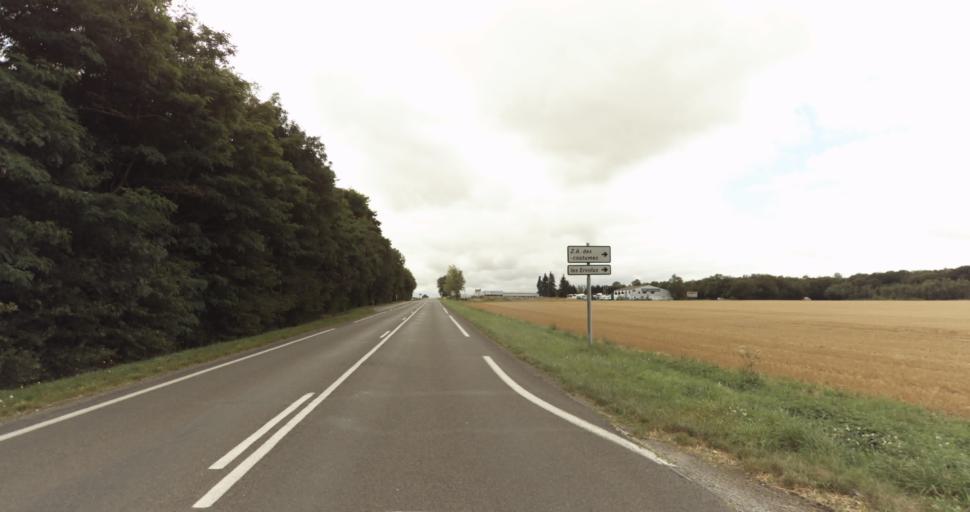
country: FR
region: Haute-Normandie
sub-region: Departement de l'Eure
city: Evreux
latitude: 48.9627
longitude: 1.1608
